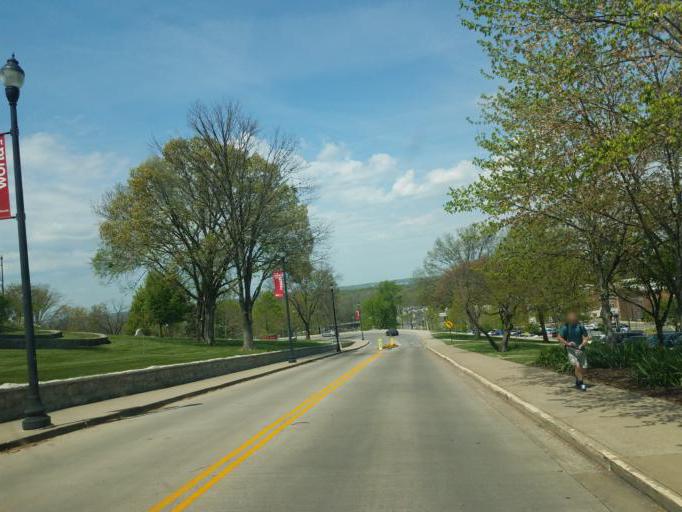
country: US
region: Kentucky
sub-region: Warren County
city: Bowling Green
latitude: 36.9882
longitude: -86.4511
